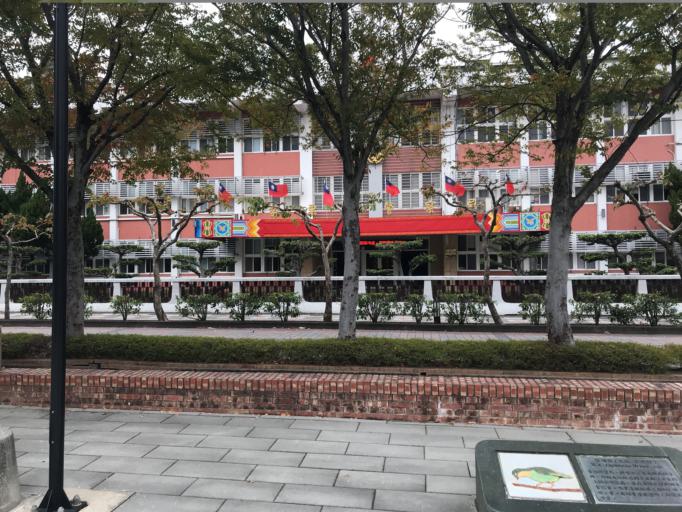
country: TW
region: Taiwan
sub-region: Miaoli
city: Miaoli
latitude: 24.5640
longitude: 120.8205
